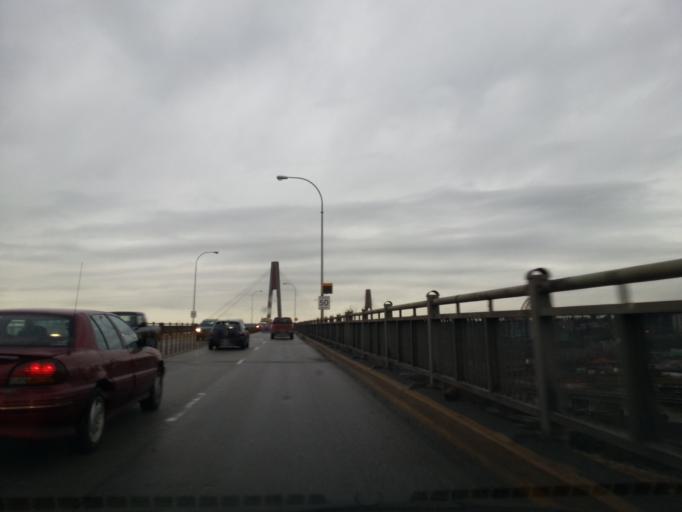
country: CA
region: British Columbia
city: New Westminster
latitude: 49.2057
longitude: -122.8850
